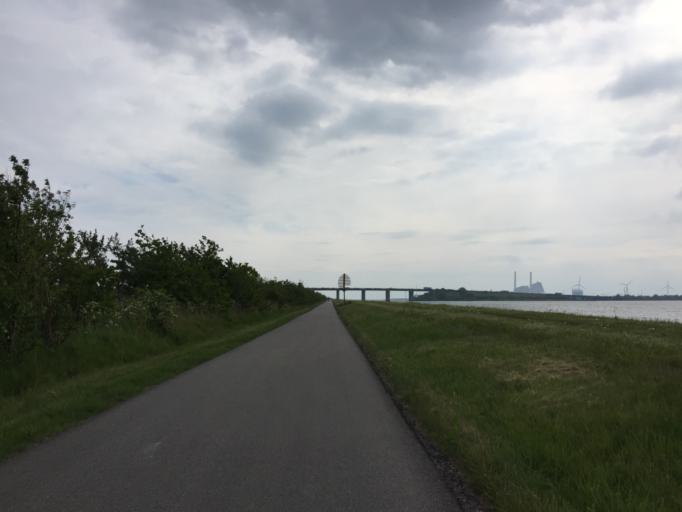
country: DK
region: Capital Region
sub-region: Hvidovre Kommune
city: Hvidovre
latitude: 55.6202
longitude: 12.5215
